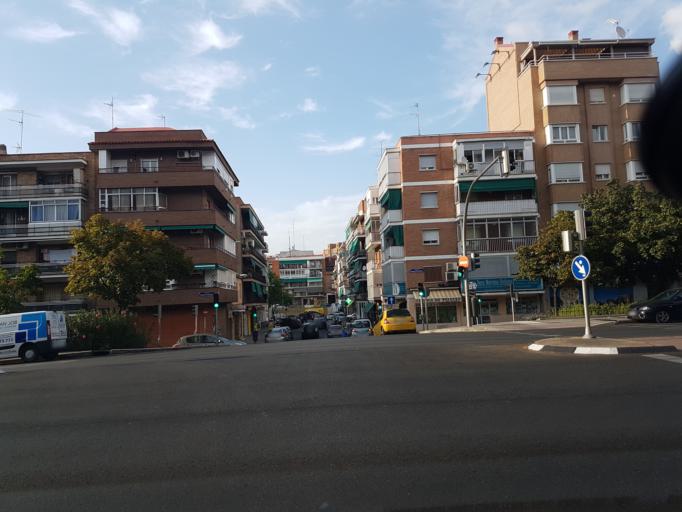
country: ES
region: Madrid
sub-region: Provincia de Madrid
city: Moratalaz
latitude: 40.4289
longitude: -3.6467
